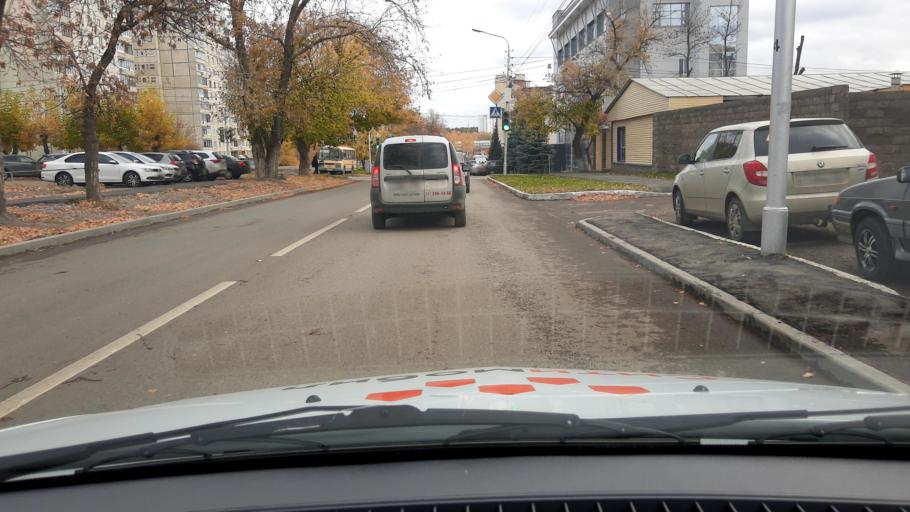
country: RU
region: Bashkortostan
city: Ufa
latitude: 54.7560
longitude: 56.0161
